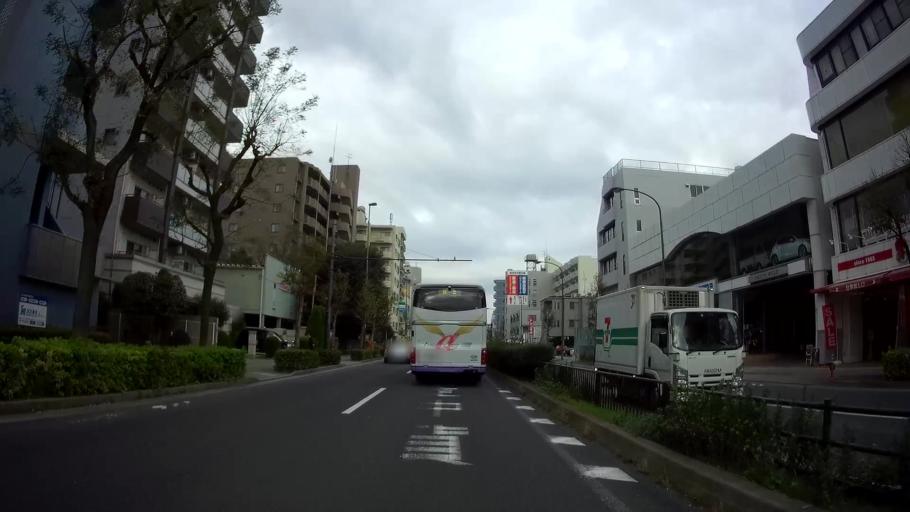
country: JP
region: Saitama
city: Wako
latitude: 35.7661
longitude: 139.6570
